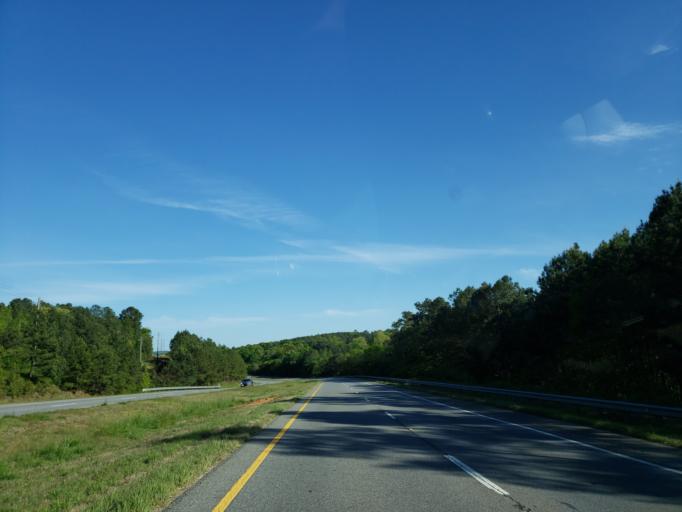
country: US
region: Georgia
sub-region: Polk County
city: Cedartown
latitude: 34.0087
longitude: -85.1776
